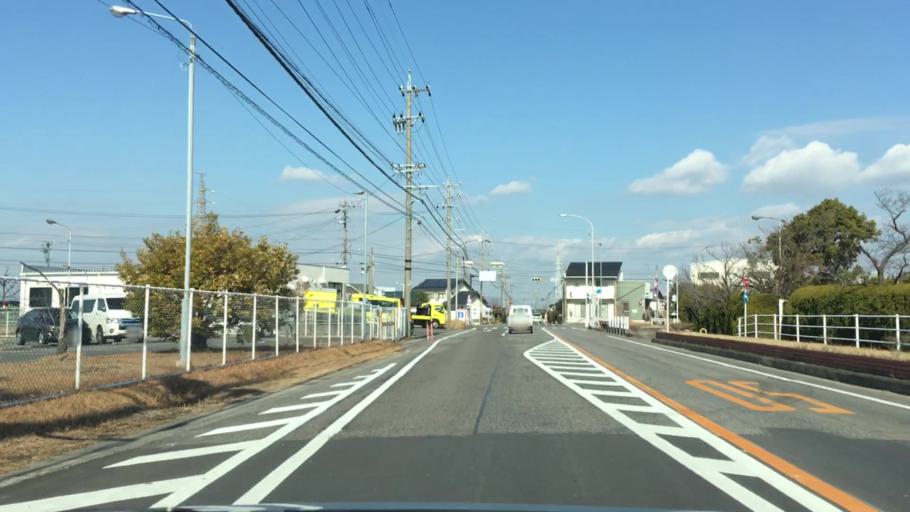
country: JP
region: Aichi
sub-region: Toyota-shi
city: Toyota
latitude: 35.0276
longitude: 137.1288
